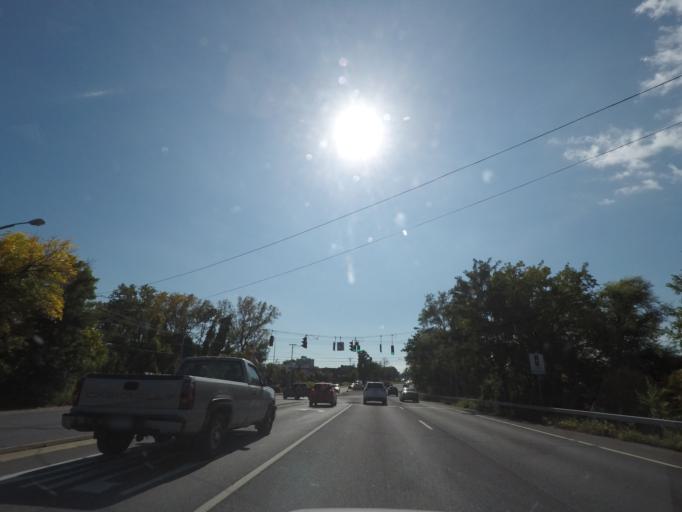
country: US
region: New York
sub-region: Albany County
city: West Albany
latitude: 42.6809
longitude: -73.7856
